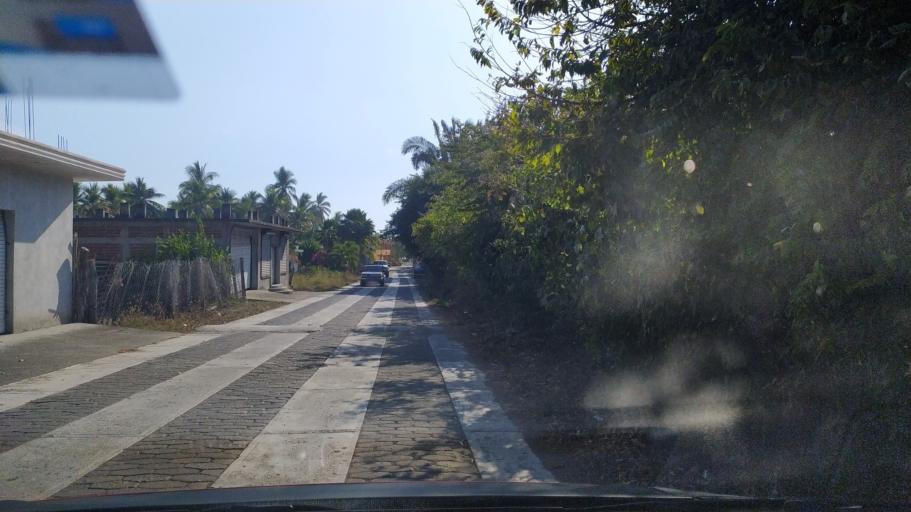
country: MX
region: Michoacan
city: Coahuayana Viejo
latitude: 18.5849
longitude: -103.6734
